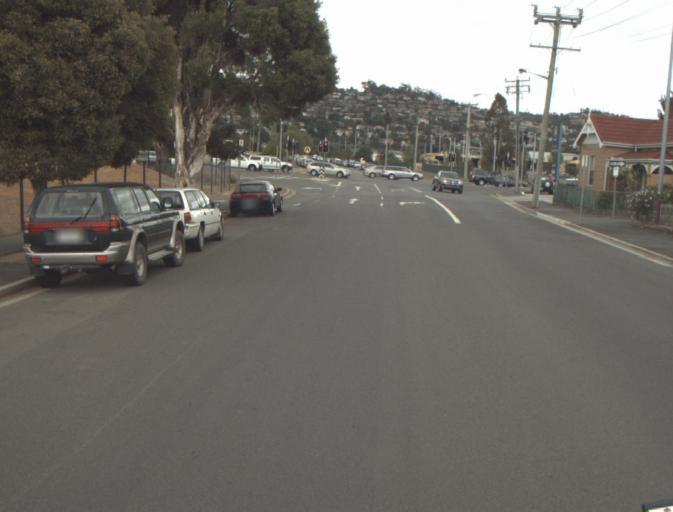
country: AU
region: Tasmania
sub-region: Launceston
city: Launceston
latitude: -41.4306
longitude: 147.1343
